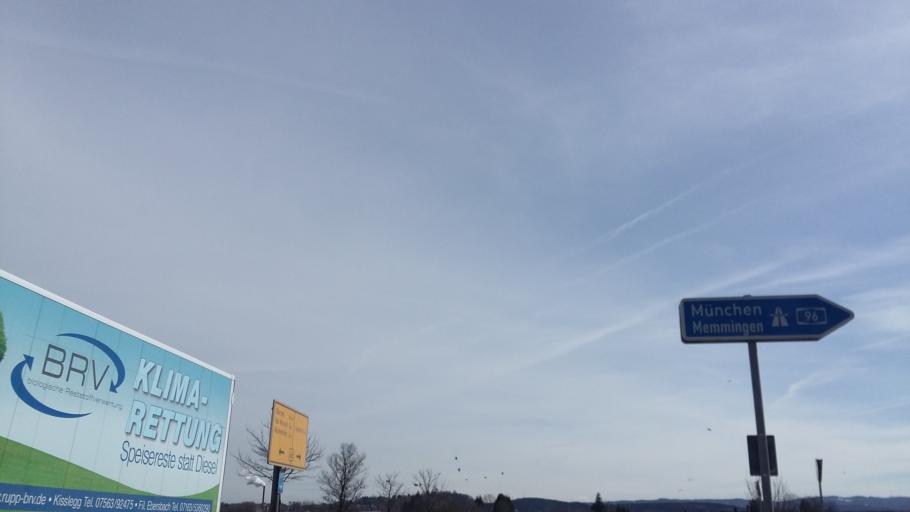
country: DE
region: Baden-Wuerttemberg
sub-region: Tuebingen Region
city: Leutkirch im Allgau
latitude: 47.8350
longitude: 9.9928
